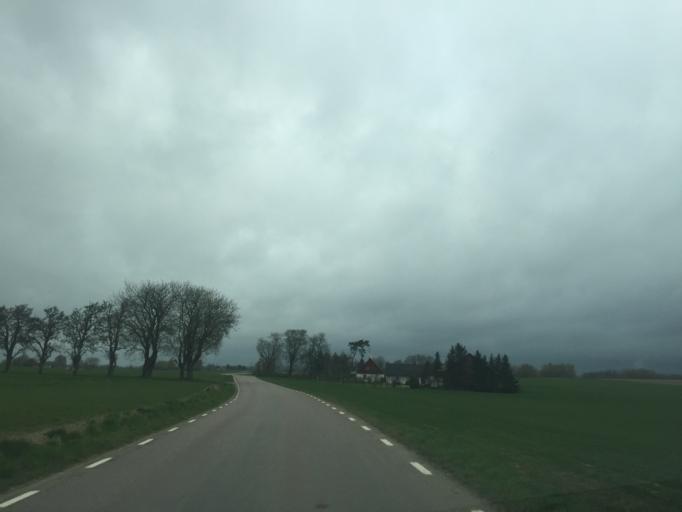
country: SE
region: Skane
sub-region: Skurups Kommun
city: Rydsgard
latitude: 55.4607
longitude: 13.6115
